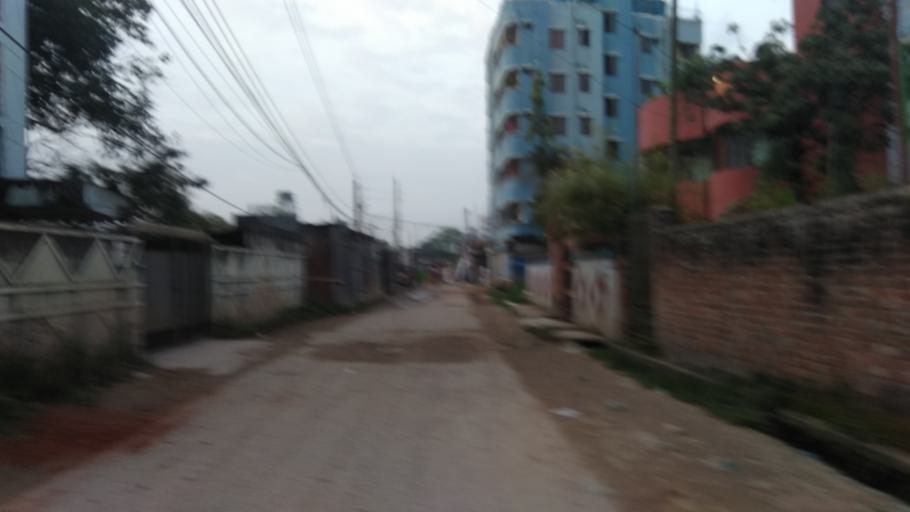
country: BD
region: Dhaka
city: Tungi
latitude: 23.8538
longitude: 90.4268
